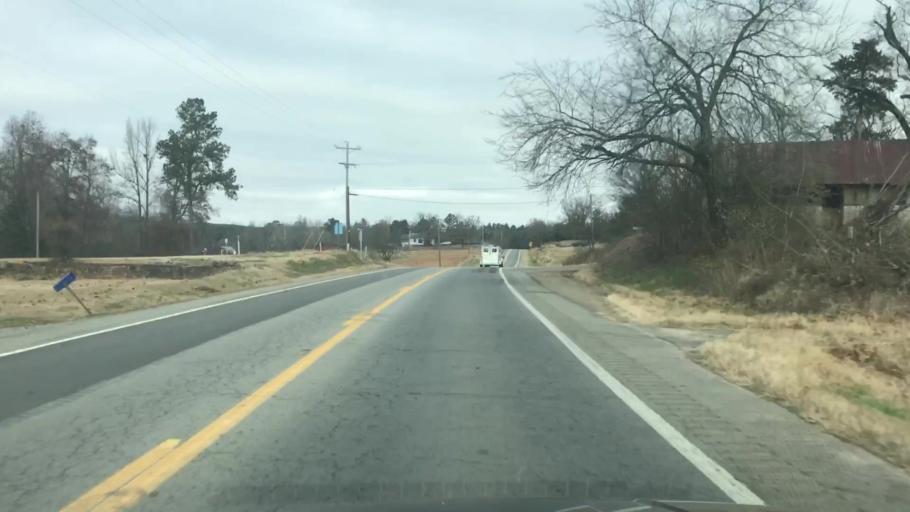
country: US
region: Arkansas
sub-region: Scott County
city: Waldron
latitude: 34.9471
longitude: -94.1043
